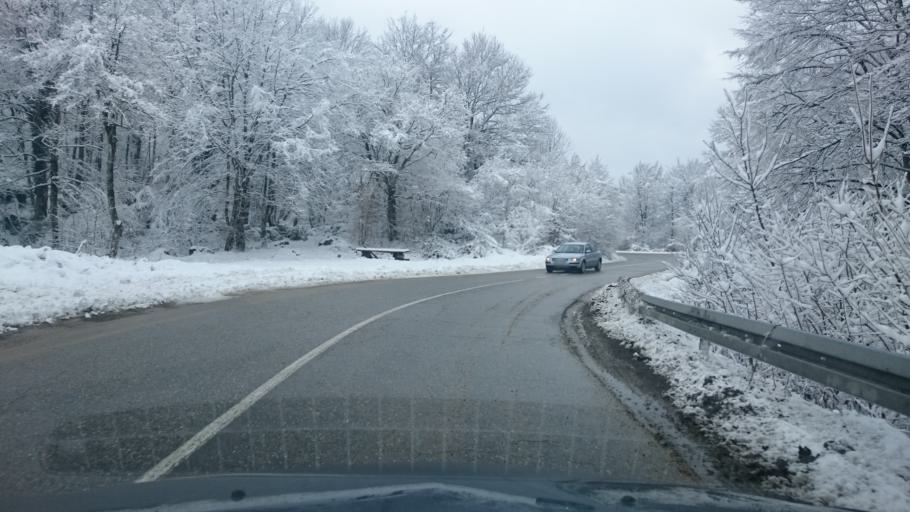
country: BA
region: Republika Srpska
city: Zivinice
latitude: 44.5412
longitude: 17.2738
